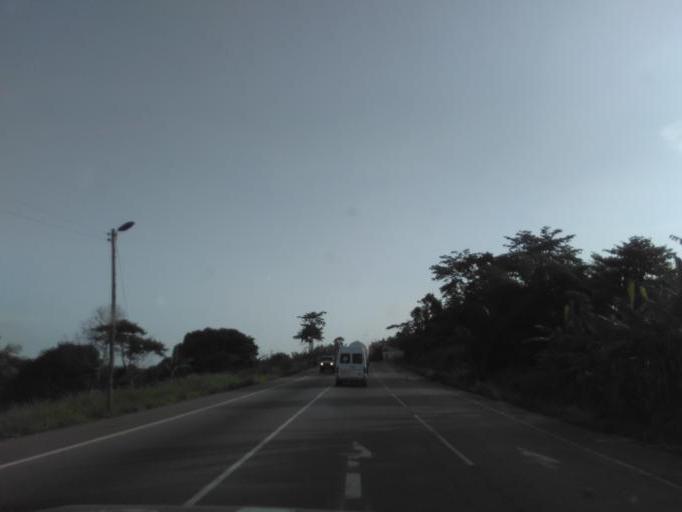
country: GH
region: Ashanti
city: Konongo
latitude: 6.6126
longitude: -1.2377
